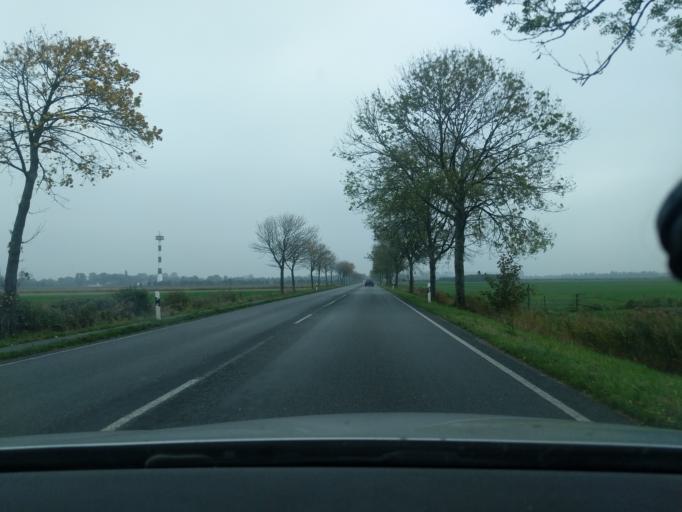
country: DE
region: Lower Saxony
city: Cuxhaven
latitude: 53.8303
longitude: 8.7480
